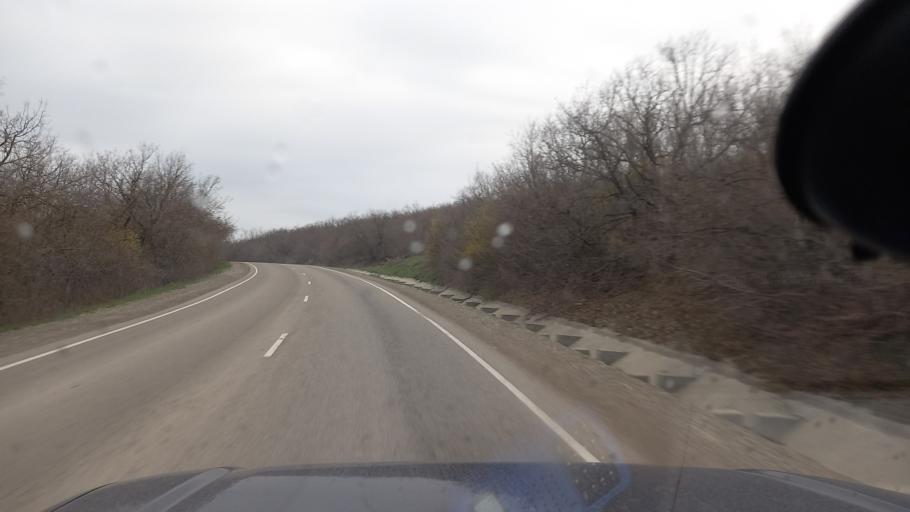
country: RU
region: Krasnodarskiy
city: Sukko
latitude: 44.8409
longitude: 37.4152
